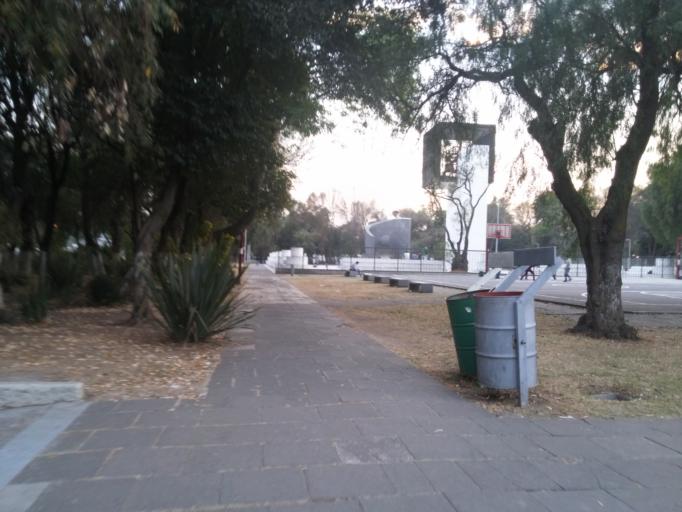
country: MX
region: Mexico
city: Colonia Lindavista
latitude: 19.5004
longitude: -99.1364
